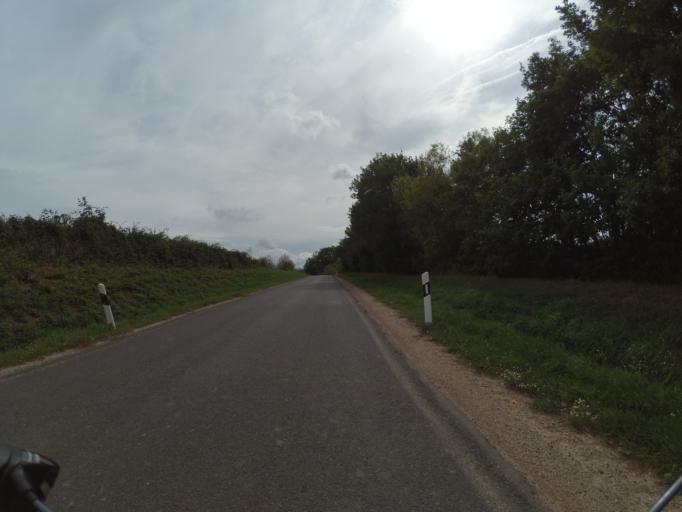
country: DE
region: Rheinland-Pfalz
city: Dodenburg
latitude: 49.9193
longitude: 6.7789
